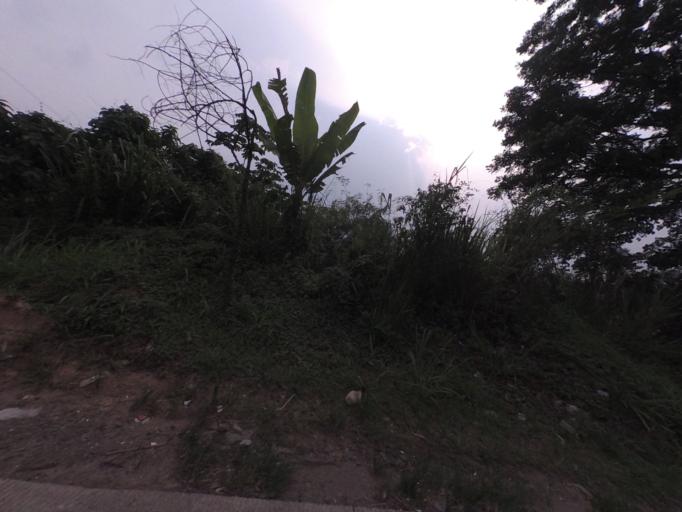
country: ID
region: West Java
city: Sidoger Lebak
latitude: -6.5600
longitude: 106.5752
